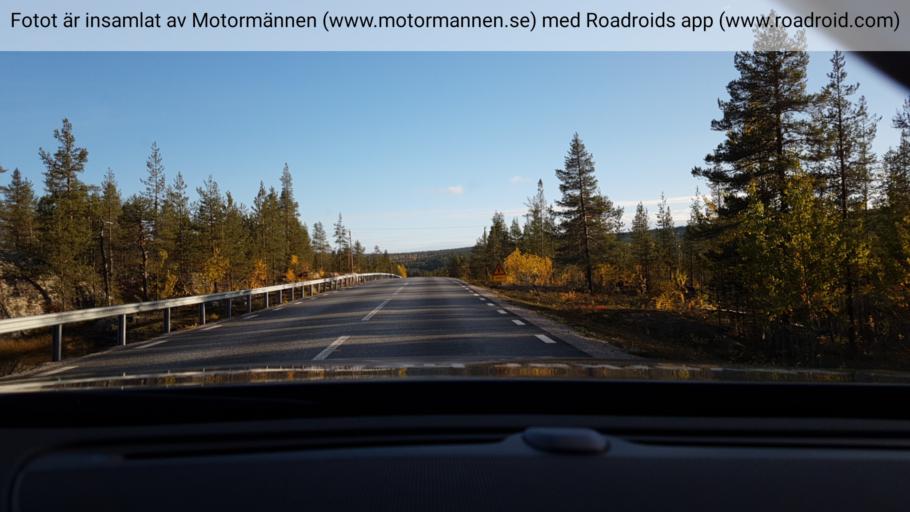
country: SE
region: Norrbotten
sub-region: Jokkmokks Kommun
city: Jokkmokk
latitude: 66.8620
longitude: 19.8182
